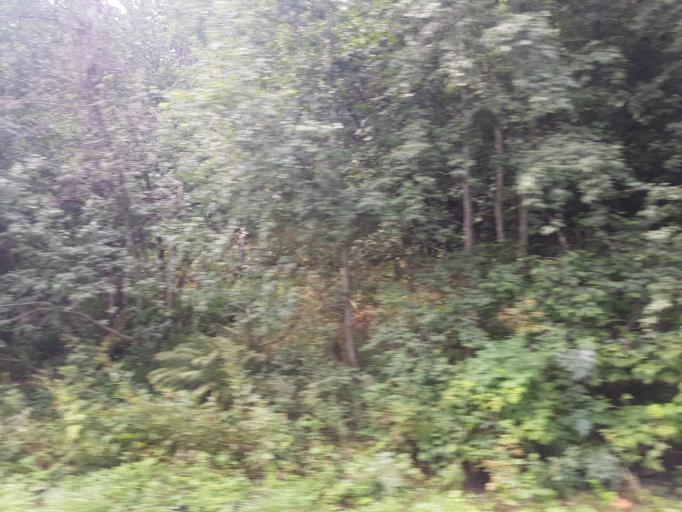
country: NO
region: Sor-Trondelag
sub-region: Trondheim
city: Trondheim
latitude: 63.3842
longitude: 10.3671
